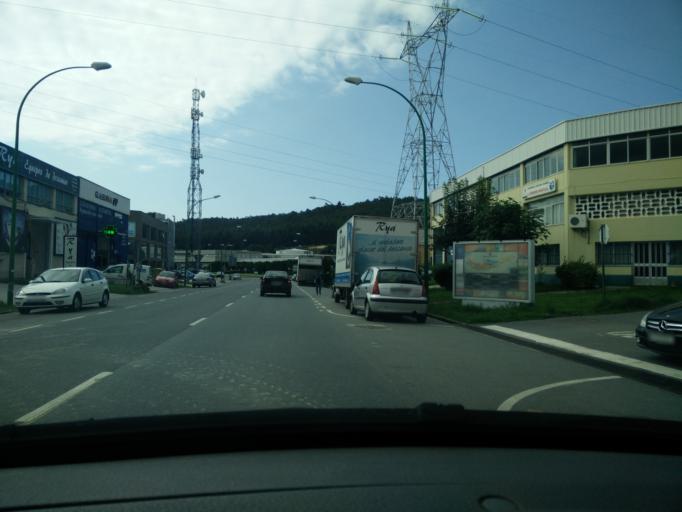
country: ES
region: Galicia
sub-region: Provincia da Coruna
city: A Coruna
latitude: 43.3308
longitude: -8.4273
